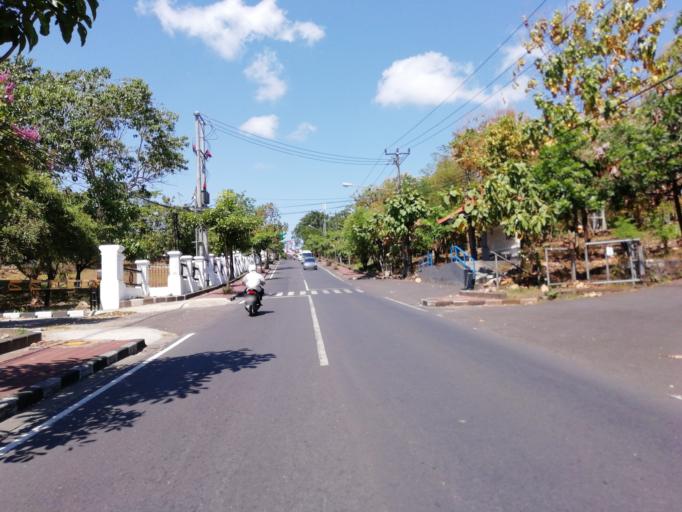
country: ID
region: Bali
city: Jimbaran
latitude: -8.7982
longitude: 115.1711
